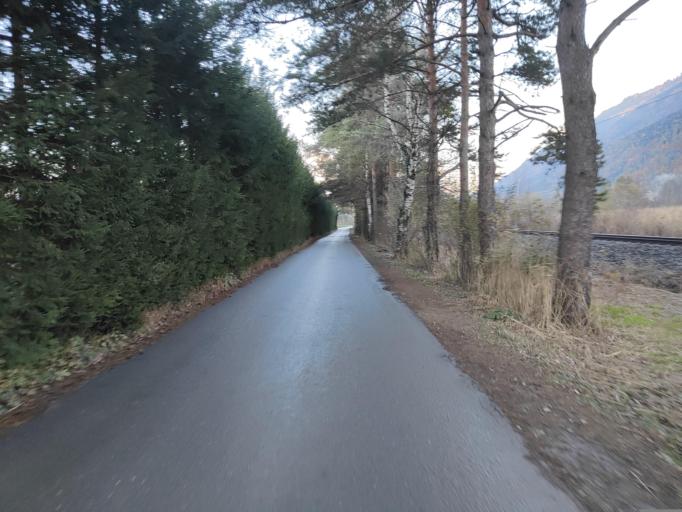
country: LI
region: Planken
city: Planken
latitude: 47.1838
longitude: 9.5233
